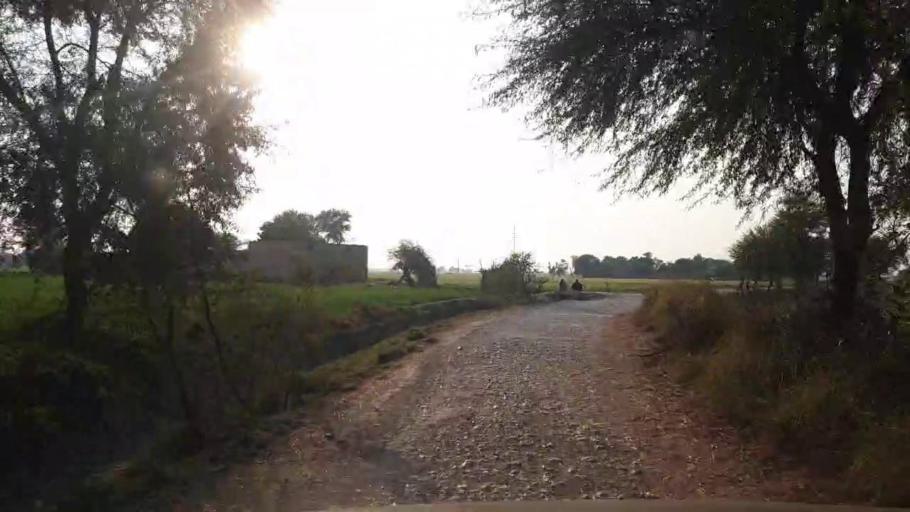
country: PK
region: Sindh
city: Shahpur Chakar
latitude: 26.1518
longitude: 68.6329
